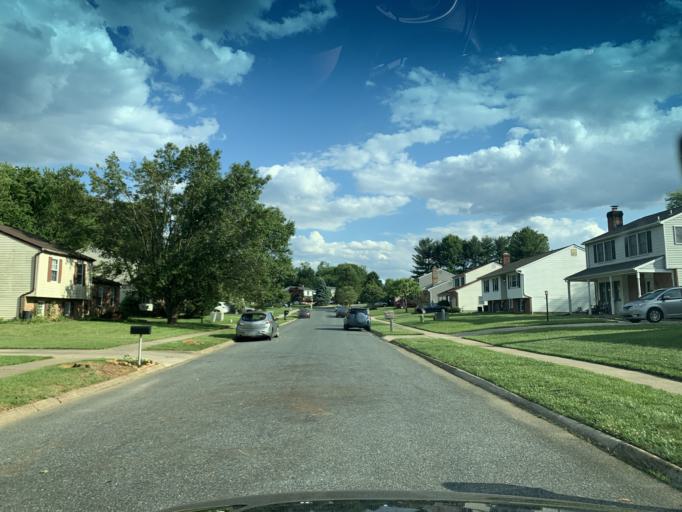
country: US
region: Maryland
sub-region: Harford County
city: Bel Air North
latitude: 39.5487
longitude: -76.3731
